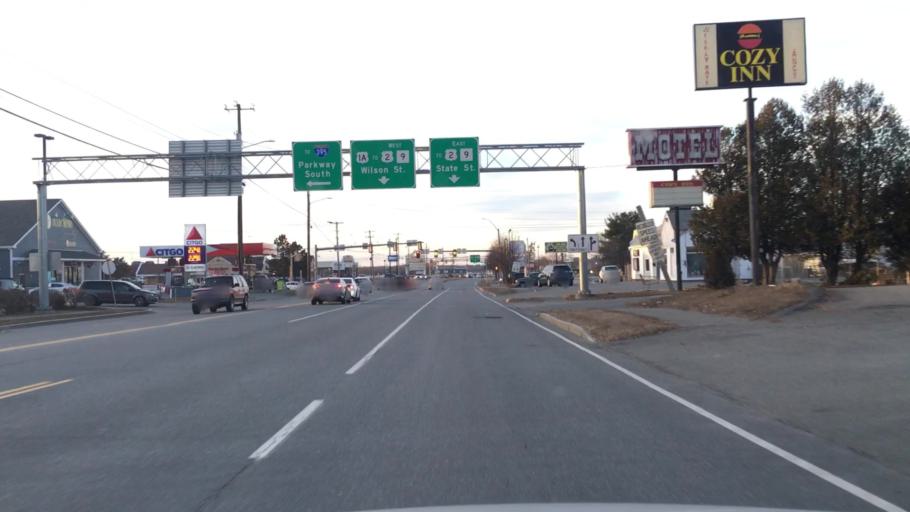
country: US
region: Maine
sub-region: Penobscot County
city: Brewer
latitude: 44.7831
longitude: -68.7488
